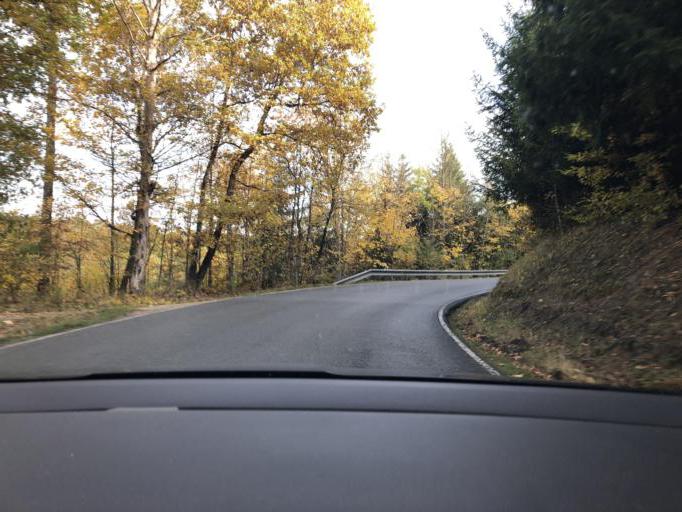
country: CZ
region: Central Bohemia
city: Divisov
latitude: 49.8004
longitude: 14.9261
